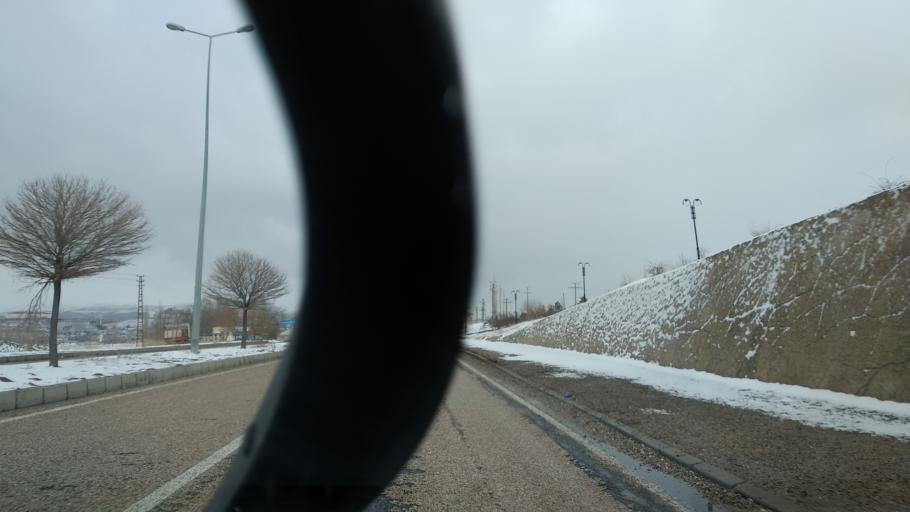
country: TR
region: Kayseri
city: Pinarbasi
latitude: 38.7122
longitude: 36.3788
